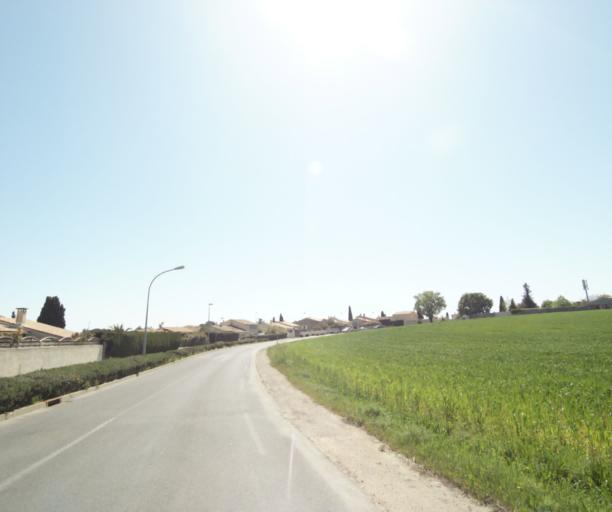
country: FR
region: Languedoc-Roussillon
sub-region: Departement de l'Herault
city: Baillargues
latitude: 43.6626
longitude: 4.0074
